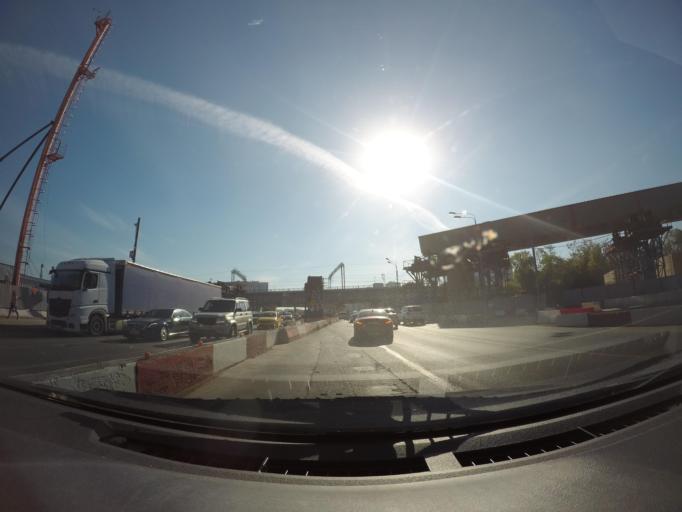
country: RU
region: Moscow
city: Tekstil'shchiki
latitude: 55.7308
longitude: 37.7252
